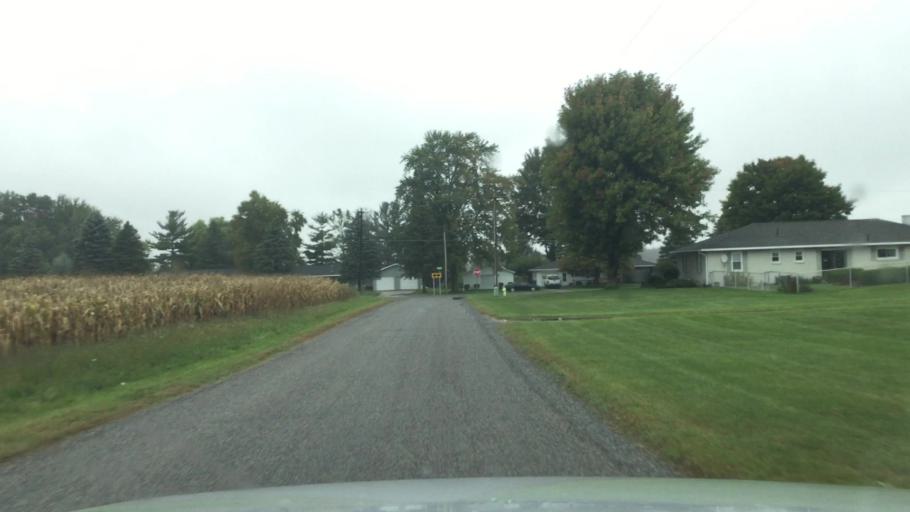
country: US
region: Michigan
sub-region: Saginaw County
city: Bridgeport
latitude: 43.3206
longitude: -83.8355
